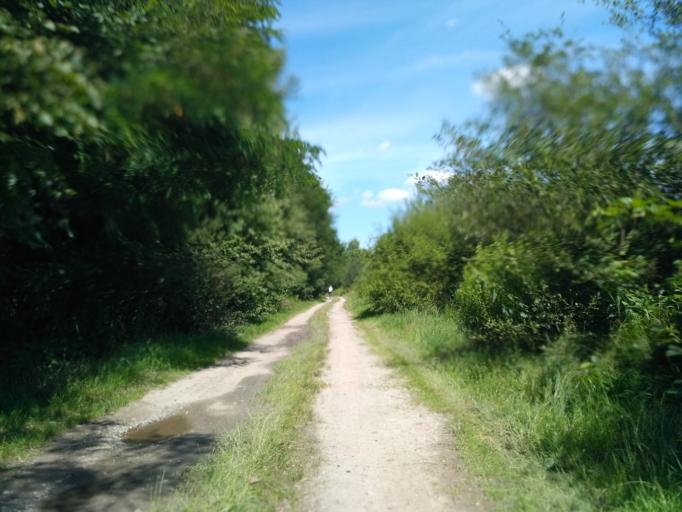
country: PL
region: Subcarpathian Voivodeship
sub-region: Powiat krosnienski
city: Kroscienko Wyzne
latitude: 49.6464
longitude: 21.8511
